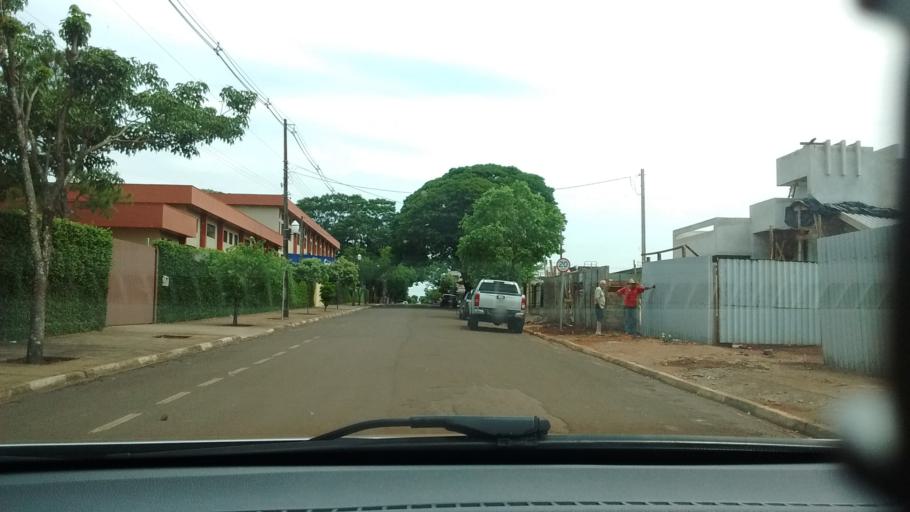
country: BR
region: Parana
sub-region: Corbelia
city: Corbelia
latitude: -24.5441
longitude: -52.9887
